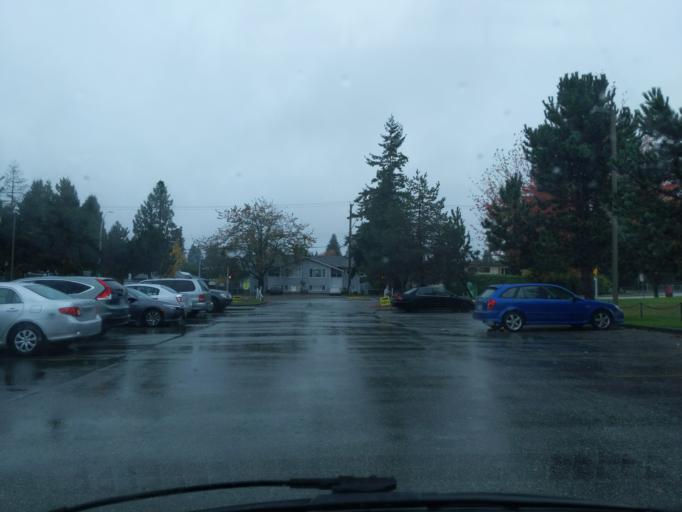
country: CA
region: British Columbia
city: New Westminster
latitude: 49.1923
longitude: -122.8593
